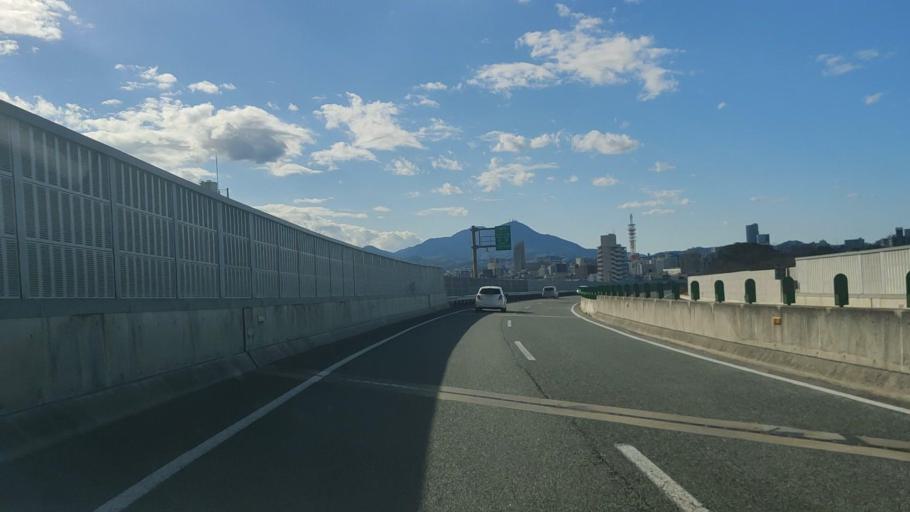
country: JP
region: Fukuoka
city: Kitakyushu
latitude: 33.8795
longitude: 130.9015
